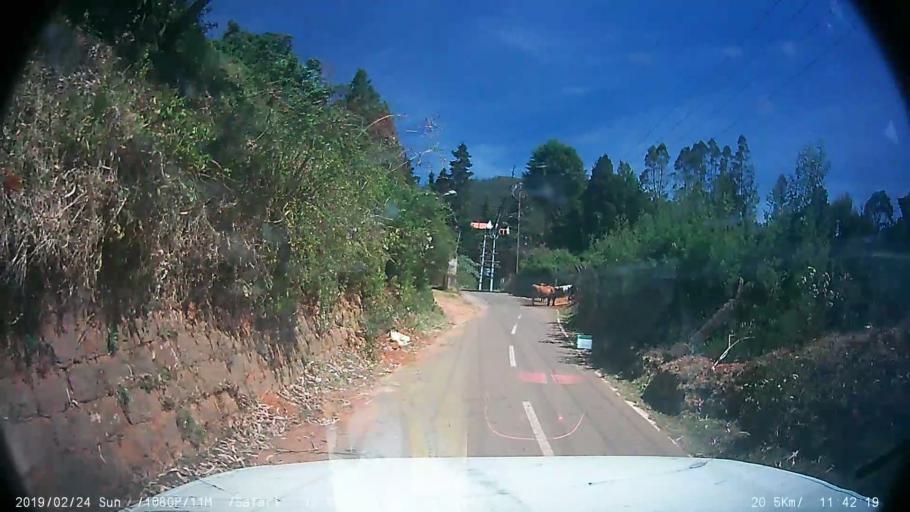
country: IN
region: Tamil Nadu
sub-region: Nilgiri
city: Ooty
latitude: 11.4199
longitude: 76.7051
